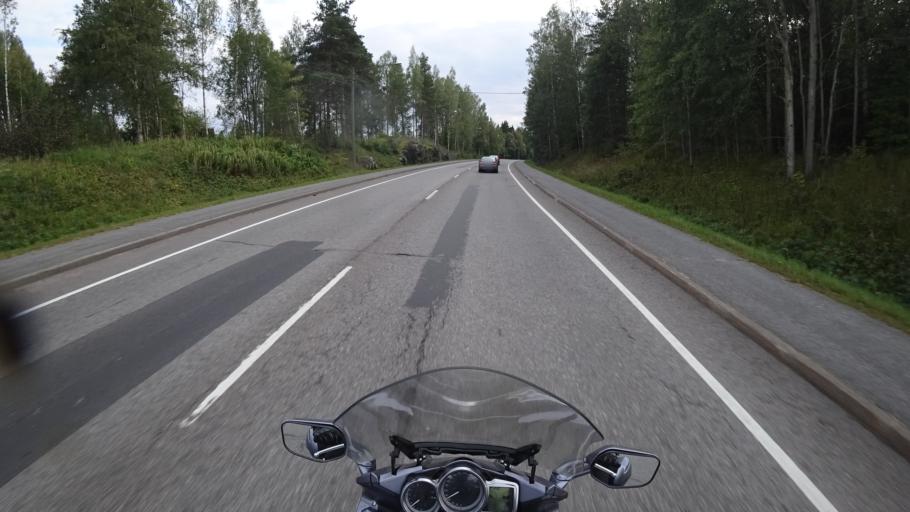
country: FI
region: Uusimaa
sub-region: Raaseporin
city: Karis
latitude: 60.0791
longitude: 23.6615
